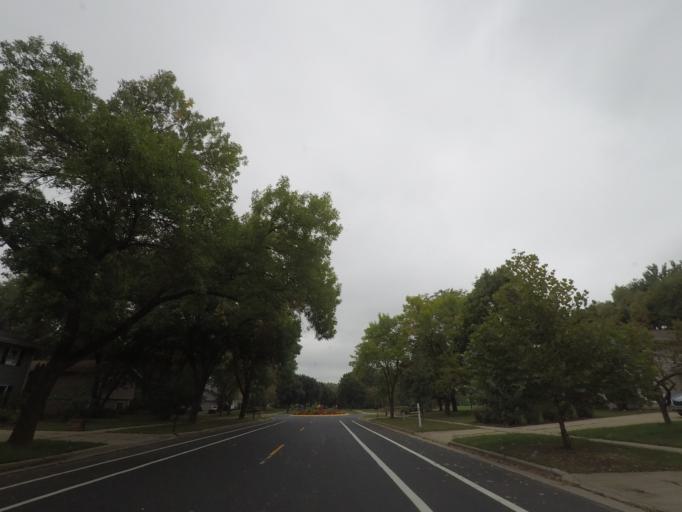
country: US
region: Wisconsin
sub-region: Dane County
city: Middleton
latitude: 43.0792
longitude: -89.5093
